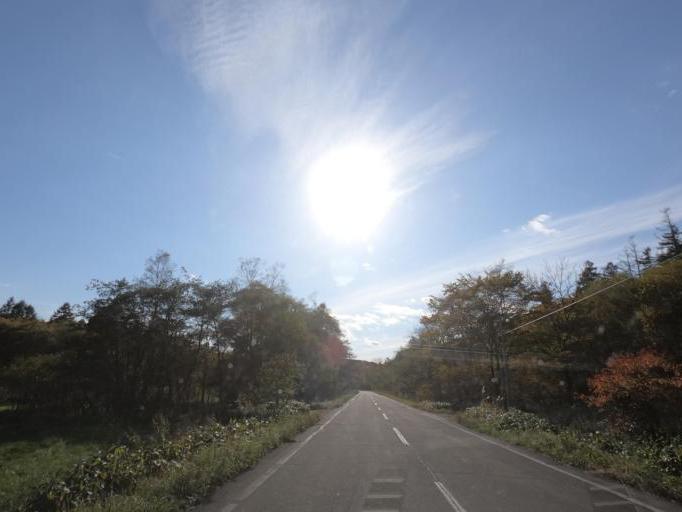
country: JP
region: Hokkaido
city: Obihiro
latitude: 42.6152
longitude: 143.3932
